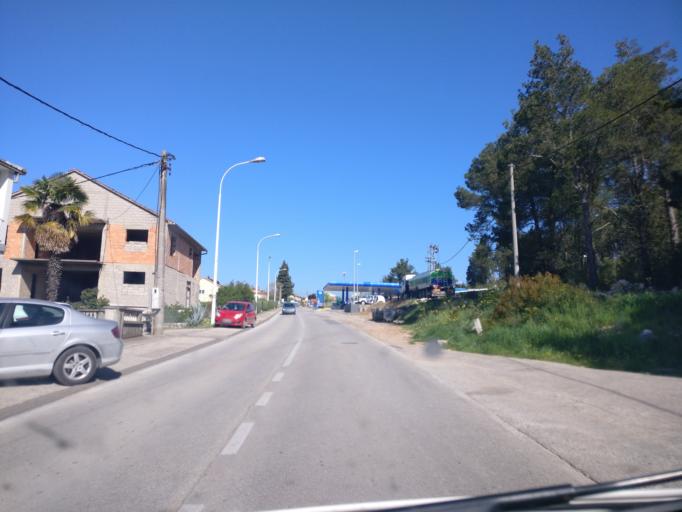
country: BA
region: Federation of Bosnia and Herzegovina
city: Capljina
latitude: 43.1204
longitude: 17.6873
